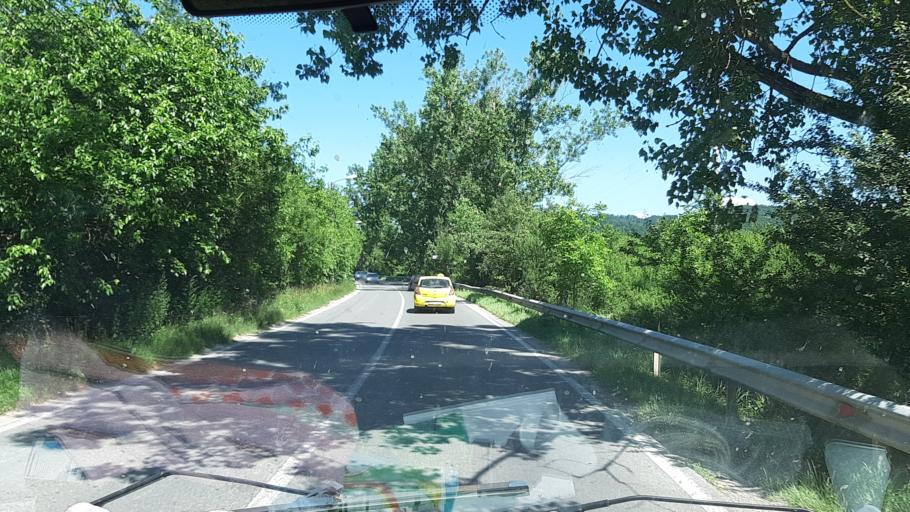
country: RO
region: Caras-Severin
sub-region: Oras Bocsa
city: Bocsa
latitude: 45.3768
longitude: 21.7498
